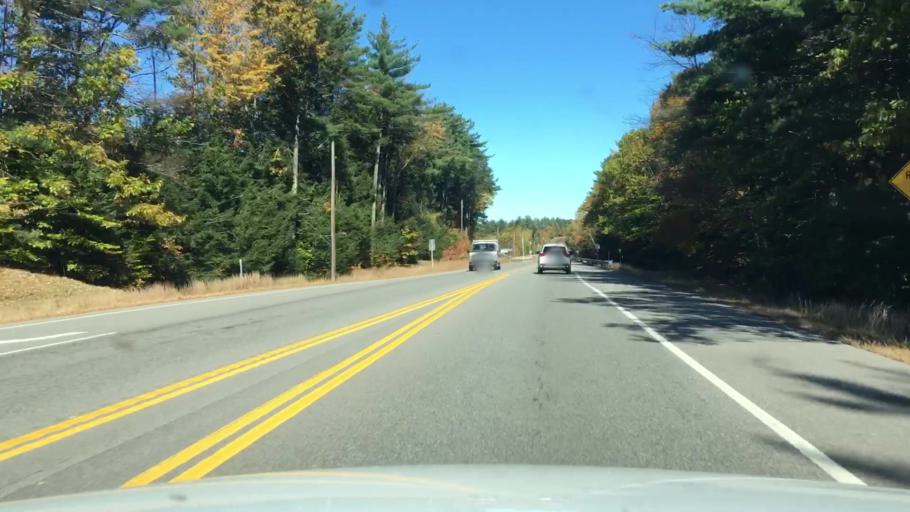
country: US
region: New Hampshire
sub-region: Carroll County
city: Sanbornville
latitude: 43.5546
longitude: -71.0405
